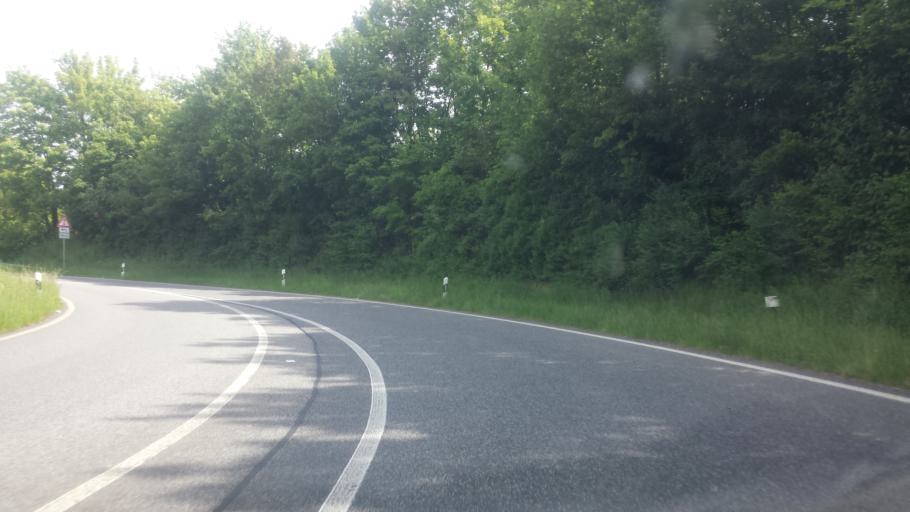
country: DE
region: Hesse
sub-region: Regierungsbezirk Darmstadt
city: Bad Vilbel
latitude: 50.1858
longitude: 8.7300
